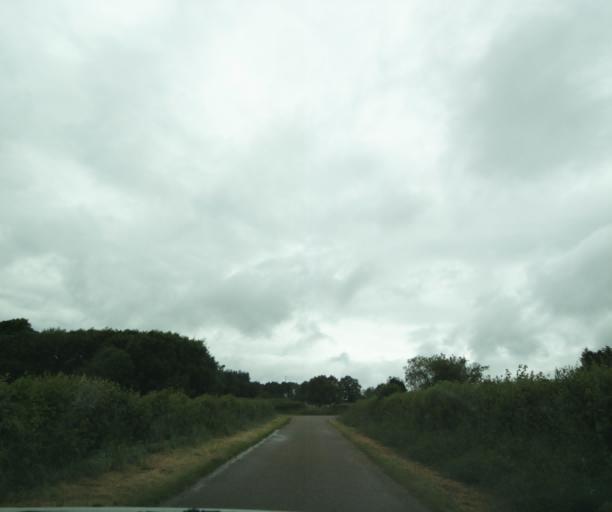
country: FR
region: Bourgogne
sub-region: Departement de Saone-et-Loire
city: Charolles
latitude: 46.4959
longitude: 4.2821
